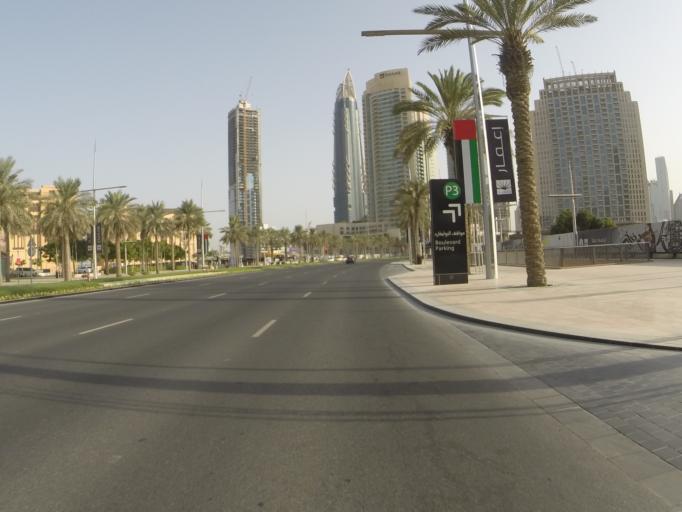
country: AE
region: Dubai
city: Dubai
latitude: 25.1937
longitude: 55.2701
